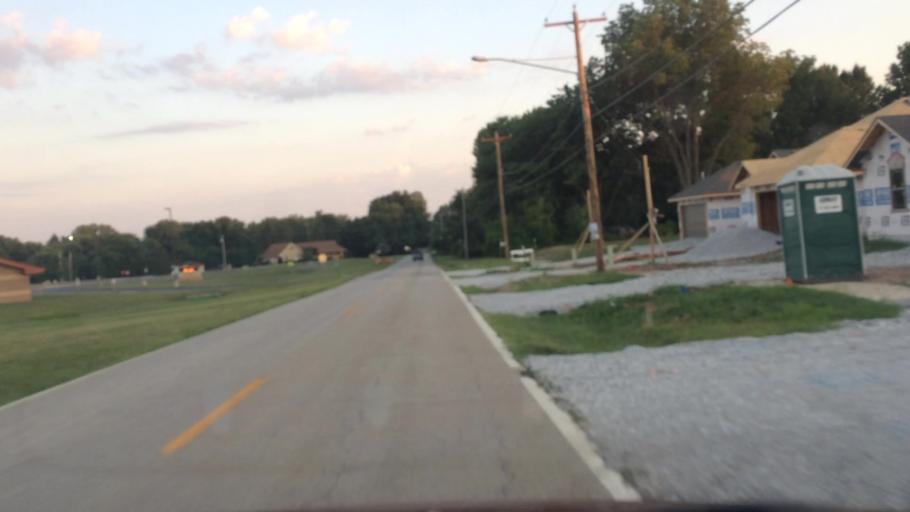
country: US
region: Missouri
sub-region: Greene County
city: Springfield
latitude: 37.2001
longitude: -93.3743
